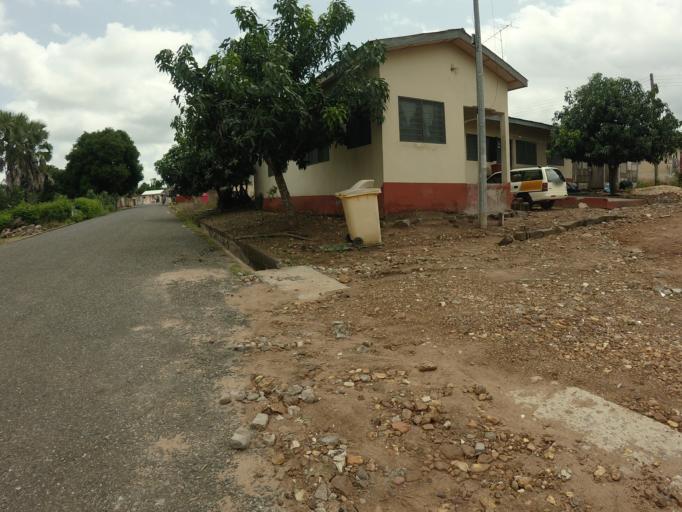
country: GH
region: Volta
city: Ho
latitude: 6.5910
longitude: 0.4761
